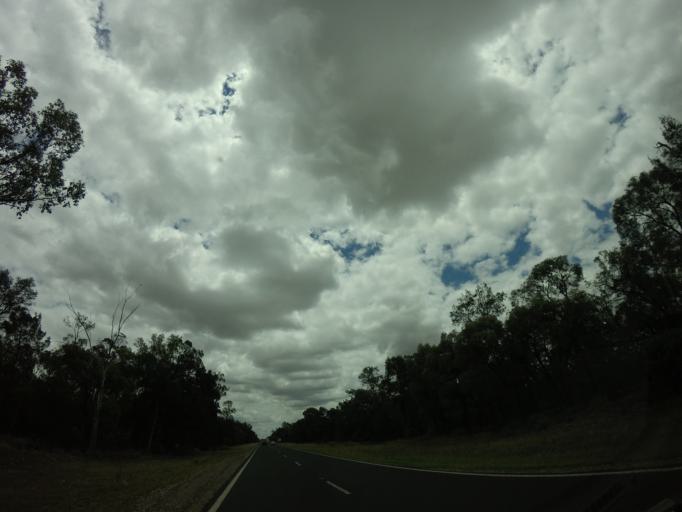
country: AU
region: Queensland
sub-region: Goondiwindi
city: Goondiwindi
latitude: -28.4099
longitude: 150.3054
